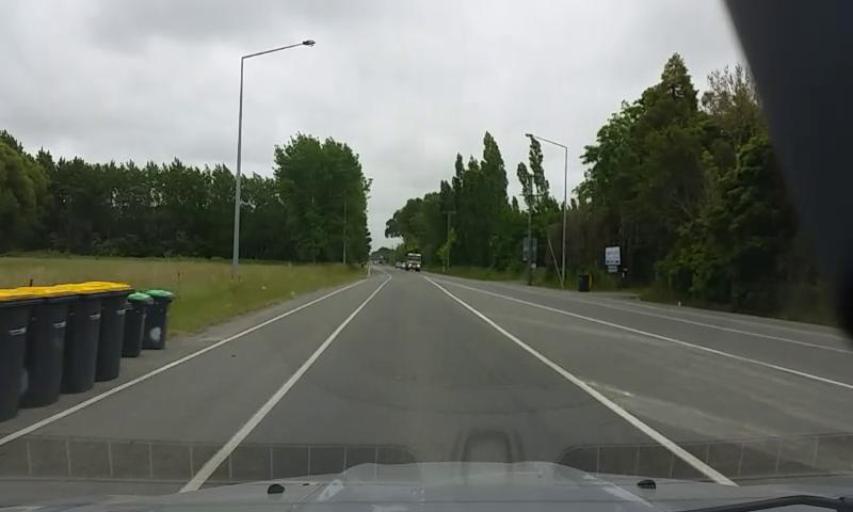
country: NZ
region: Canterbury
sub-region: Selwyn District
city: Prebbleton
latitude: -43.5177
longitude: 172.5254
